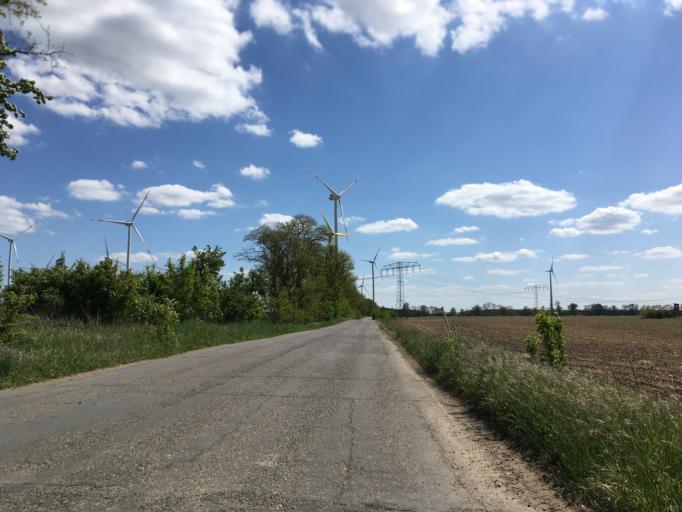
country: DE
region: Brandenburg
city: Rudnitz
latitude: 52.6938
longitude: 13.6692
